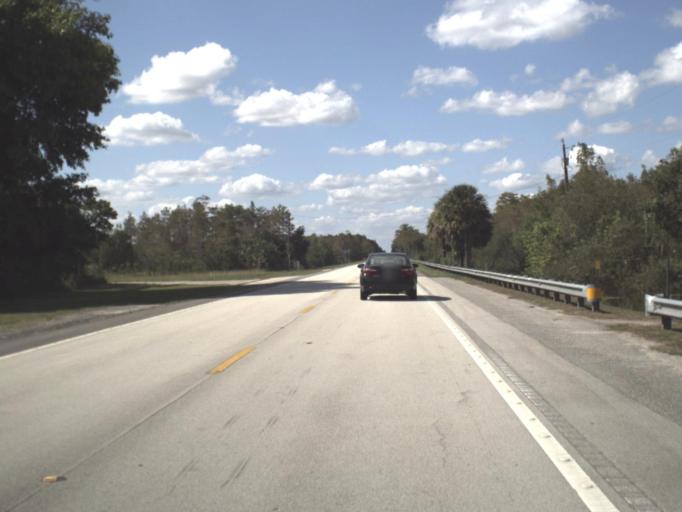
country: US
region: Florida
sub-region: Miami-Dade County
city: Kendall West
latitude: 25.8187
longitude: -80.8886
